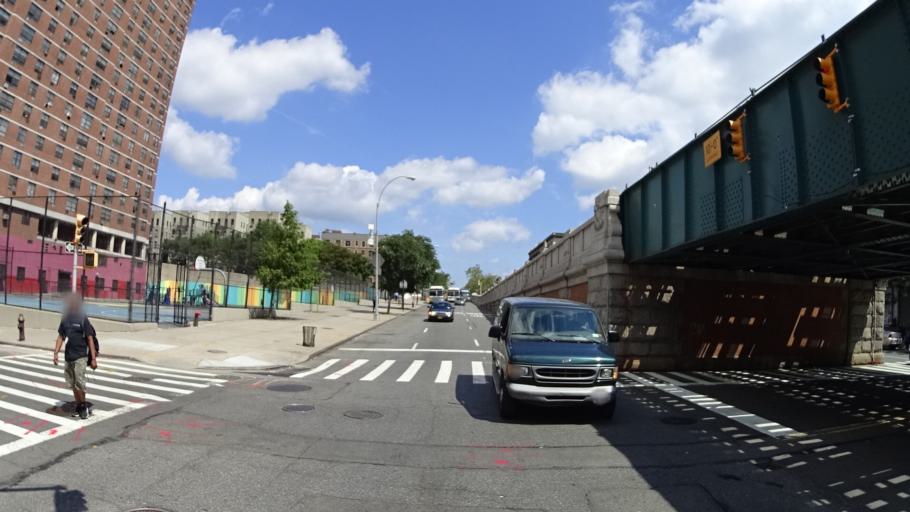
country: US
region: New Jersey
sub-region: Bergen County
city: Edgewater
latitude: 40.8189
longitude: -73.9561
